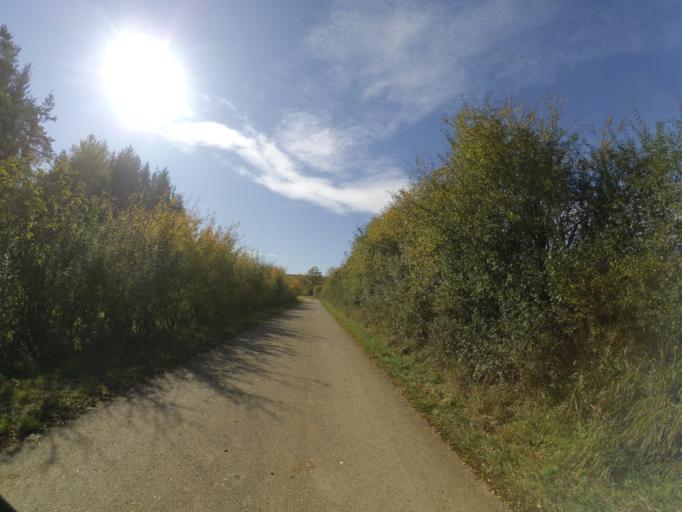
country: DE
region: Baden-Wuerttemberg
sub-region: Tuebingen Region
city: Westerstetten
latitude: 48.5422
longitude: 9.9615
